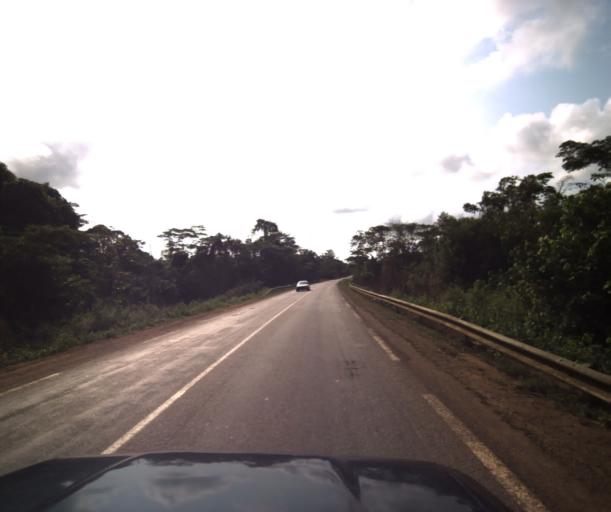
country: CM
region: Littoral
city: Edea
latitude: 3.9448
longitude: 10.0437
